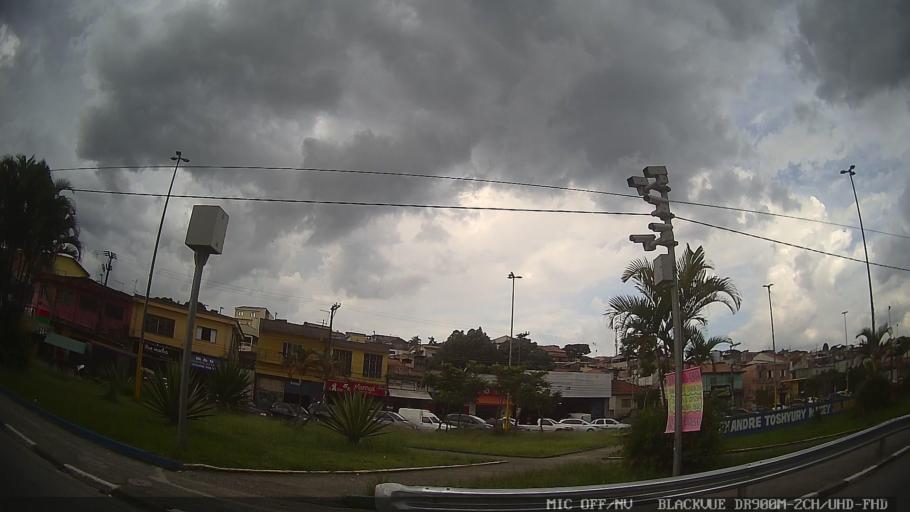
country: BR
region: Sao Paulo
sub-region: Maua
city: Maua
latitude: -23.6661
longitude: -46.4301
